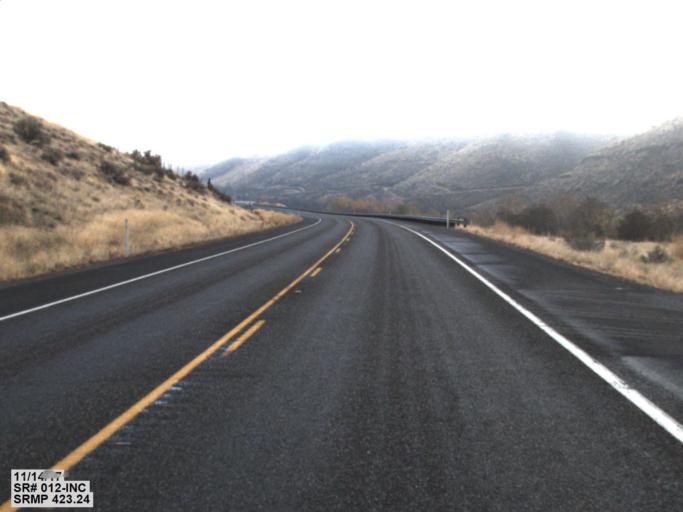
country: US
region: Washington
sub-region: Asotin County
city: Clarkston Heights-Vineland
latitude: 46.4035
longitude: -117.2465
